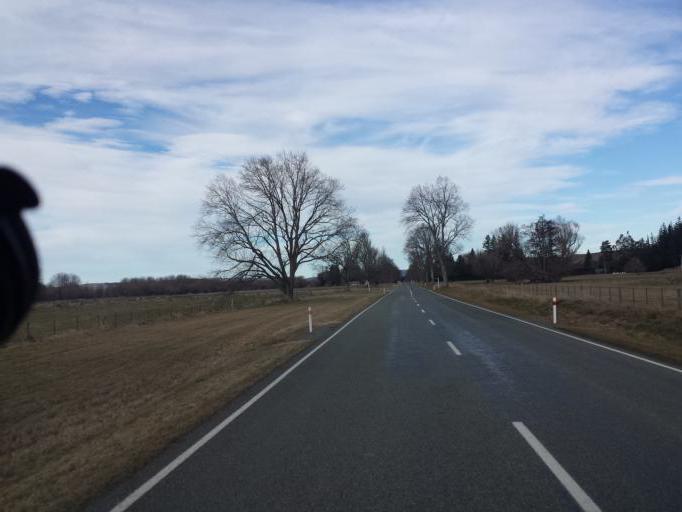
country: NZ
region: Canterbury
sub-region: Timaru District
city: Pleasant Point
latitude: -44.0378
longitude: 170.7505
